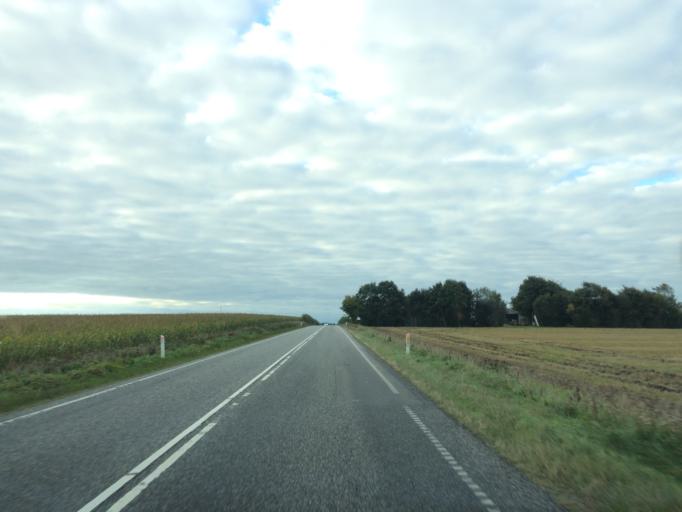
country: DK
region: Central Jutland
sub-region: Ringkobing-Skjern Kommune
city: Skjern
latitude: 55.9978
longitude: 8.5048
